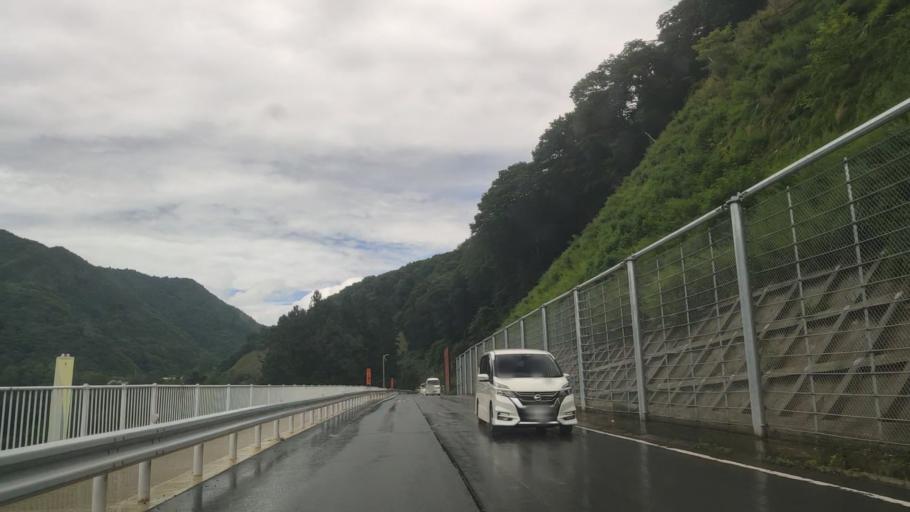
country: JP
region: Gunma
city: Numata
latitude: 36.7649
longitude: 139.2284
